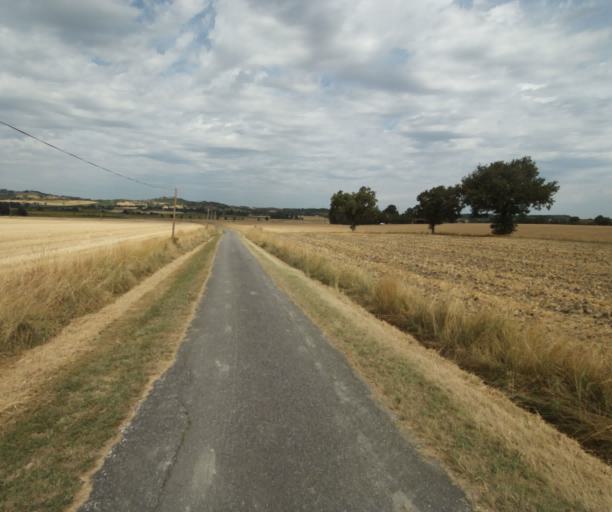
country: FR
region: Midi-Pyrenees
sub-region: Departement de la Haute-Garonne
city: Saint-Felix-Lauragais
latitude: 43.4336
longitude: 1.9265
